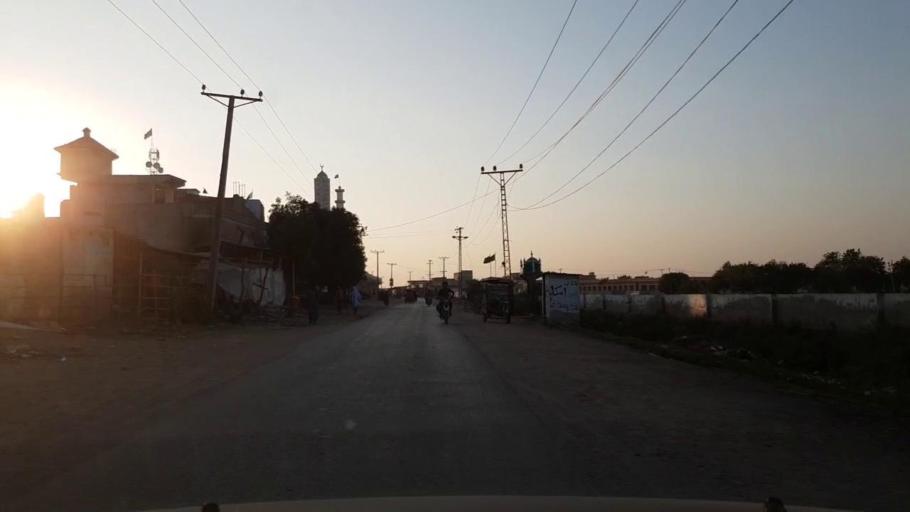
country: PK
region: Sindh
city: Thatta
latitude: 24.6070
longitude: 68.0749
